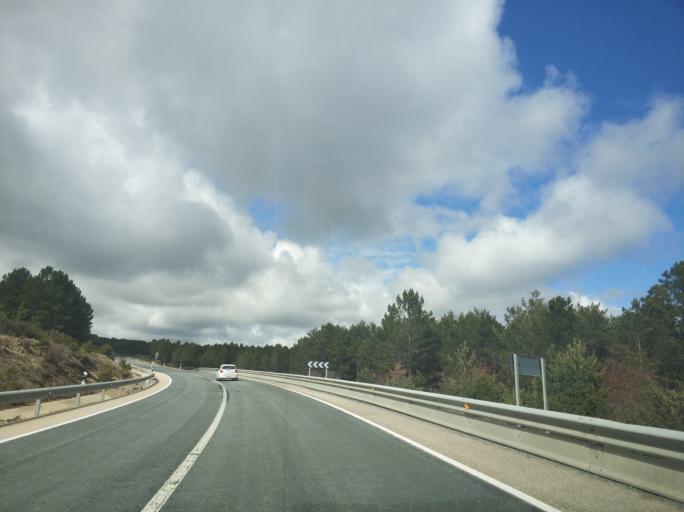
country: ES
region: Castille and Leon
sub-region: Provincia de Soria
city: Muriel Viejo
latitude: 41.8221
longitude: -2.9402
